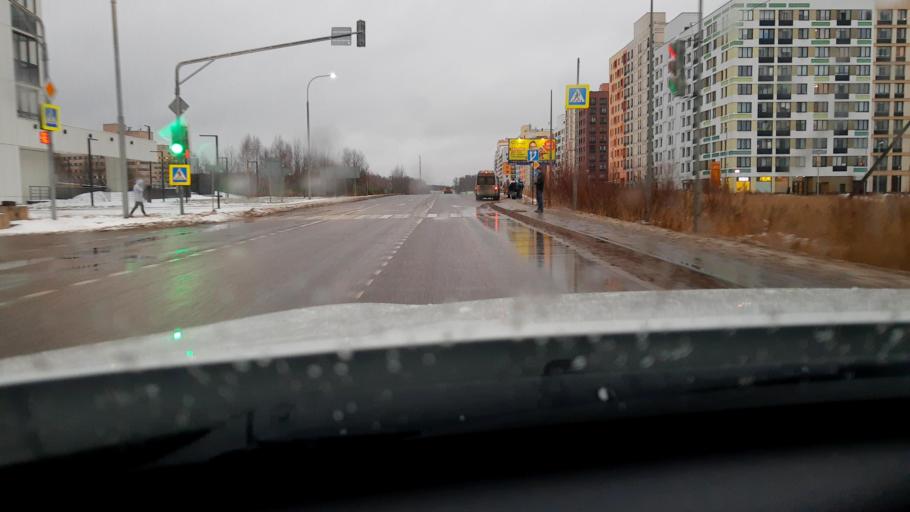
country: RU
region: Moskovskaya
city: Krasnogorsk
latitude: 55.8700
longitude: 37.3197
